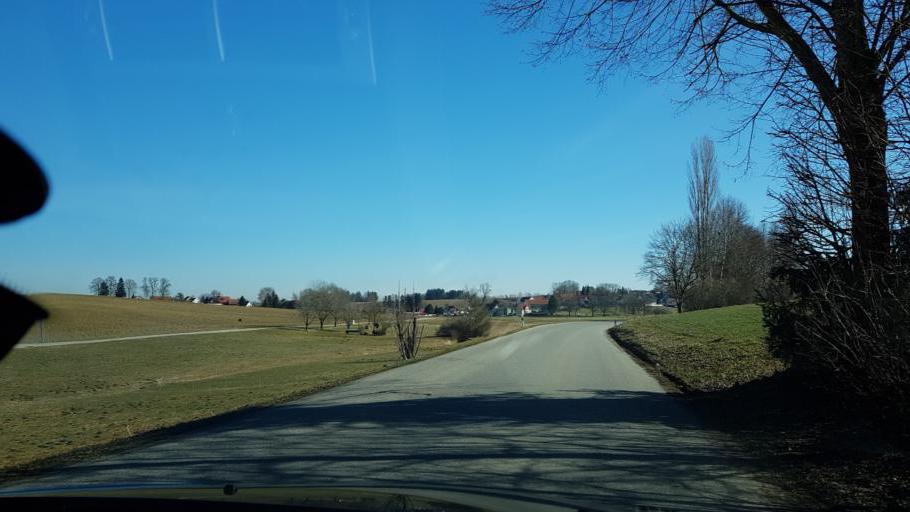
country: DE
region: Bavaria
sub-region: Upper Bavaria
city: Oberschweinbach
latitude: 48.2408
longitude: 11.1463
